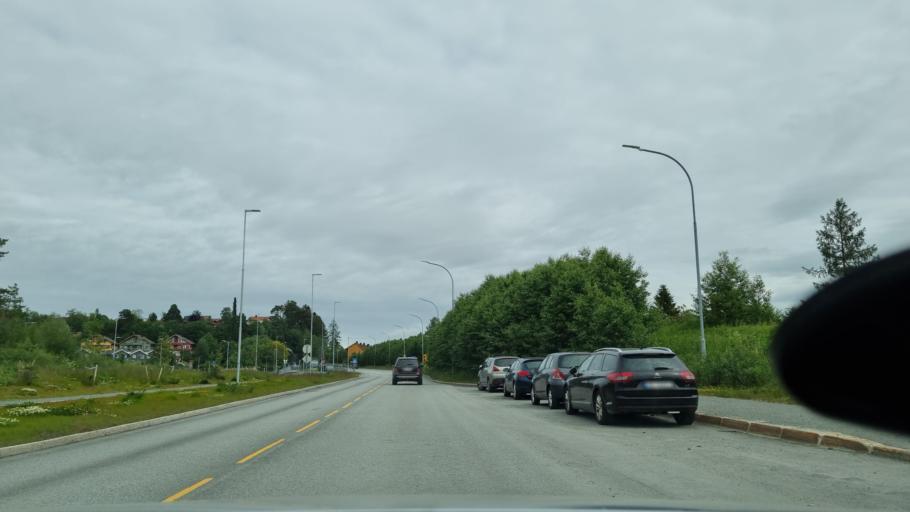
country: NO
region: Sor-Trondelag
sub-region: Melhus
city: Melhus
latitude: 63.3487
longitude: 10.3309
